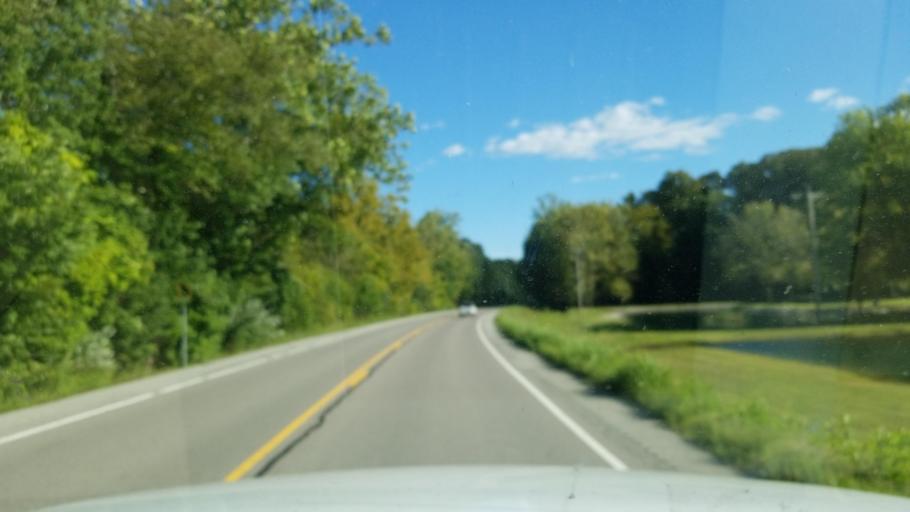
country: US
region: Illinois
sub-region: Saline County
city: Harrisburg
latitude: 37.5938
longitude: -88.4539
